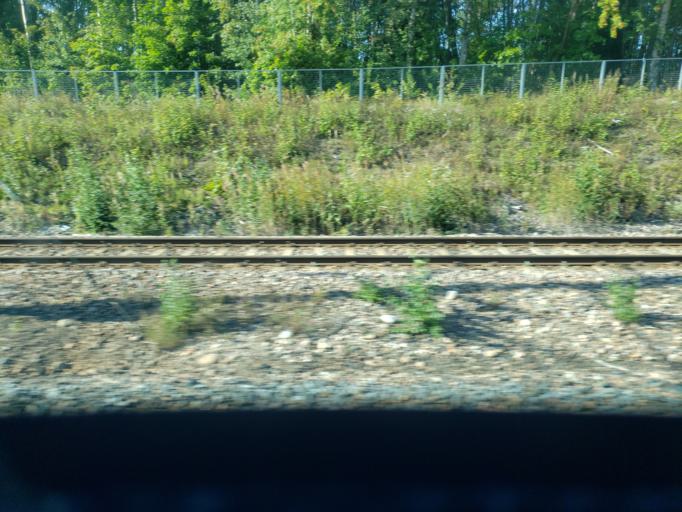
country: FI
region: Uusimaa
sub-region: Helsinki
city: Helsinki
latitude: 60.2227
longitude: 24.9532
